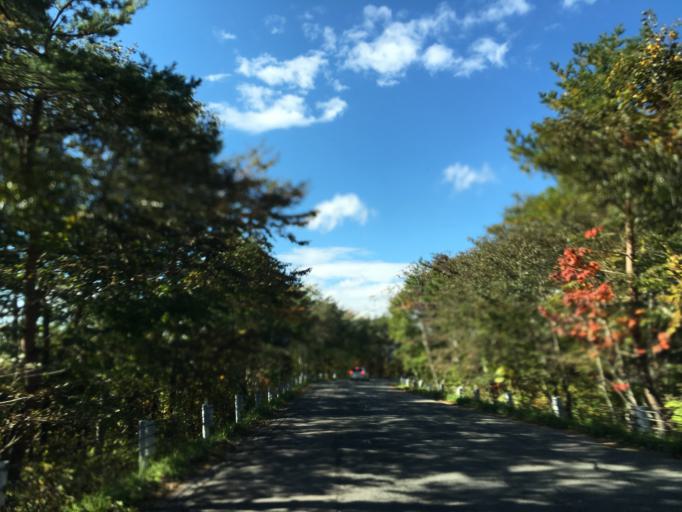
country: JP
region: Fukushima
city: Inawashiro
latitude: 37.6082
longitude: 140.2307
